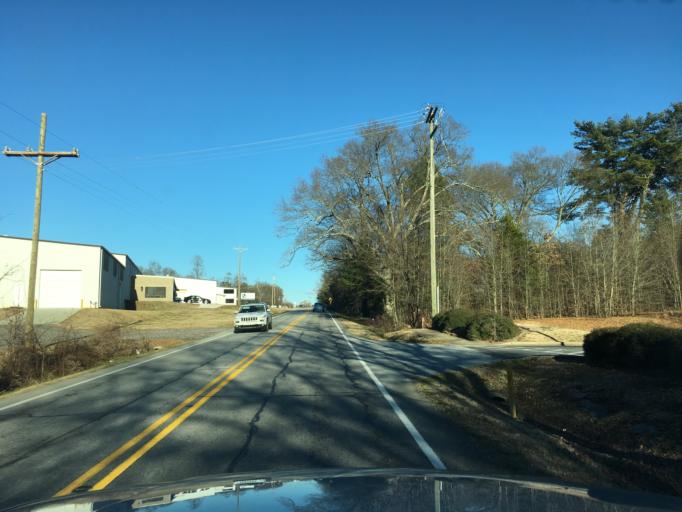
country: US
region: South Carolina
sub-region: Greenville County
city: Taylors
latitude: 34.9190
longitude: -82.2598
